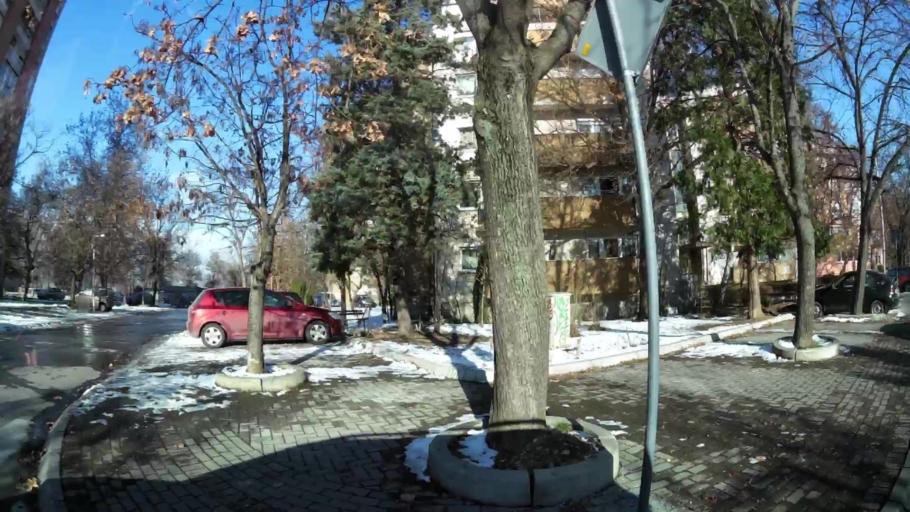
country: MK
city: Krushopek
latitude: 42.0074
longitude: 21.3876
